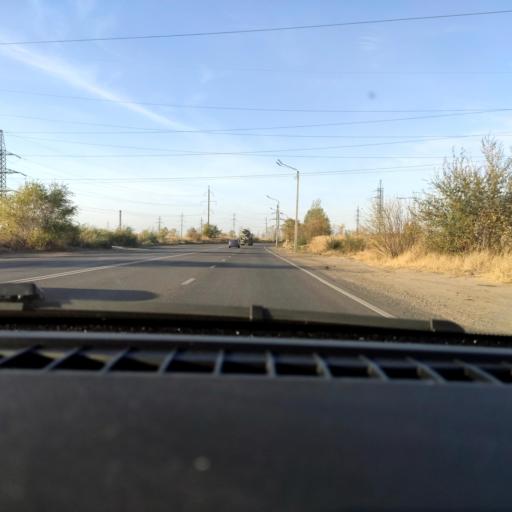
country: RU
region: Voronezj
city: Maslovka
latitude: 51.6230
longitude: 39.2781
